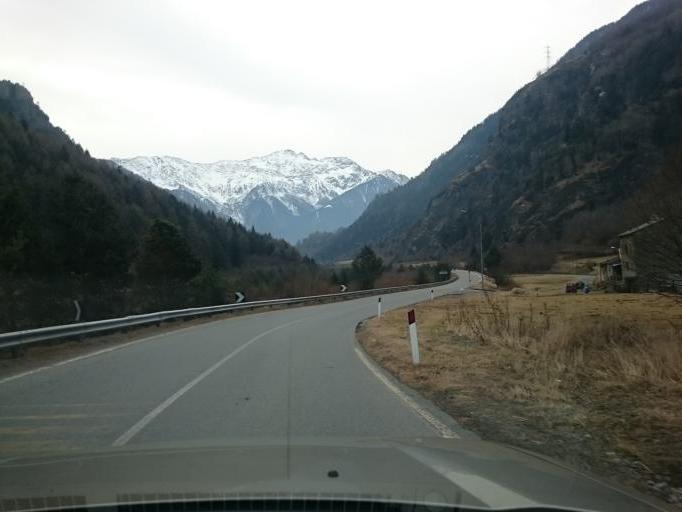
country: IT
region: Lombardy
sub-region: Provincia di Sondrio
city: Sondalo
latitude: 46.3677
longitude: 10.3564
